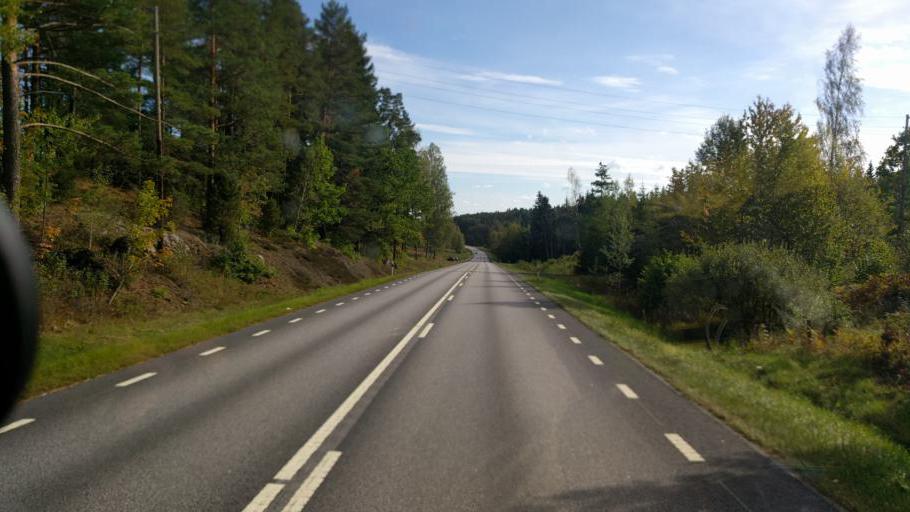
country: SE
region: OEstergoetland
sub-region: Kinda Kommun
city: Kisa
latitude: 57.9179
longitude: 15.6823
